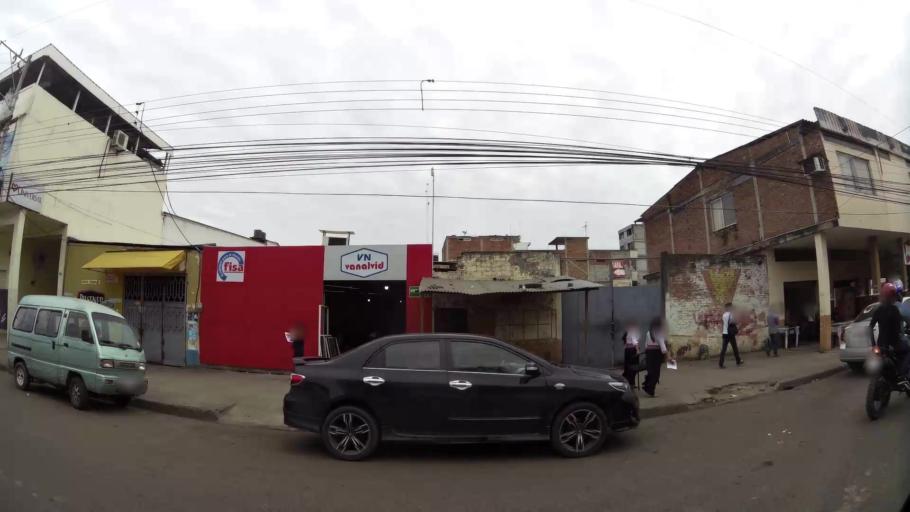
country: EC
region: El Oro
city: Machala
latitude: -3.2560
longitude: -79.9590
